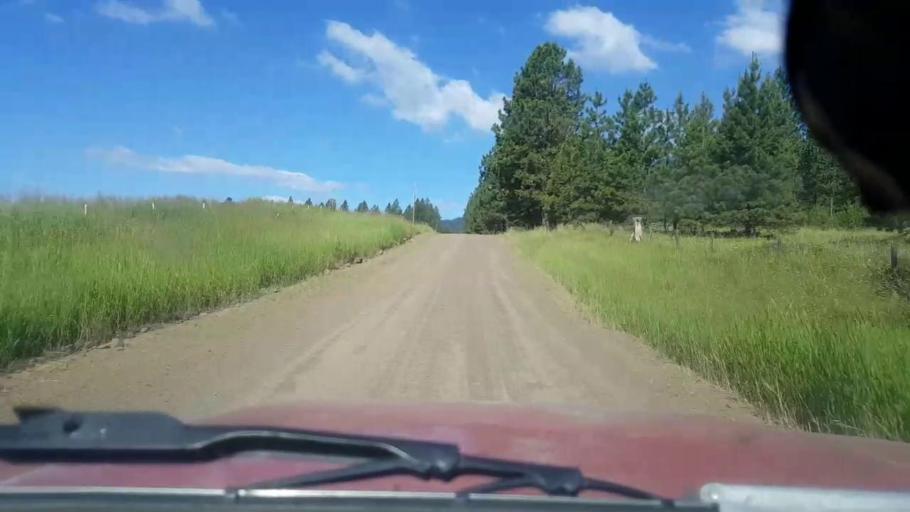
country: US
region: Washington
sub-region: Garfield County
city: Pomeroy
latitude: 46.0370
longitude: -117.4231
